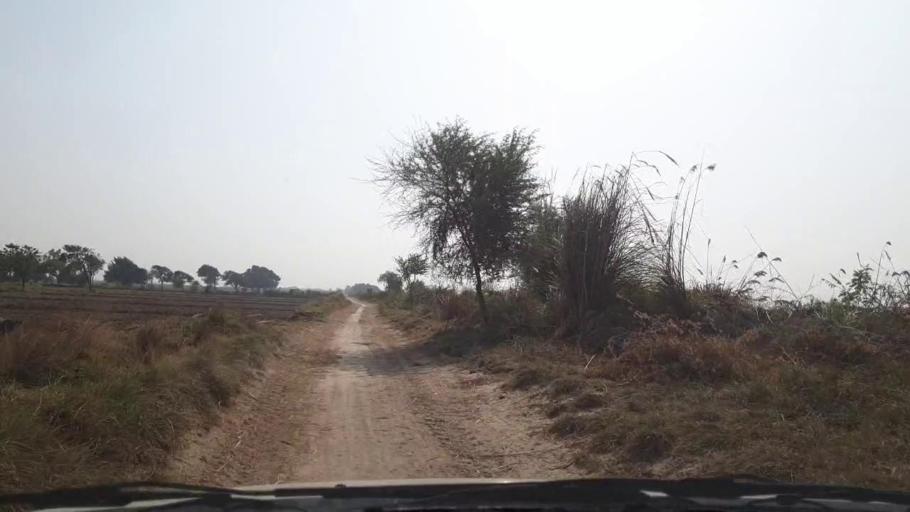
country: PK
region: Sindh
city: Tando Muhammad Khan
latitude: 25.0759
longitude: 68.3626
